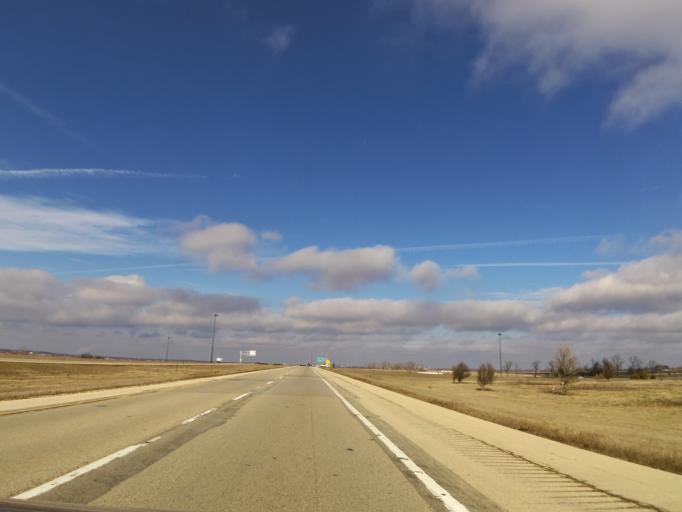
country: US
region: Illinois
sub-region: Ogle County
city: Rochelle
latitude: 41.9013
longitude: -89.0187
